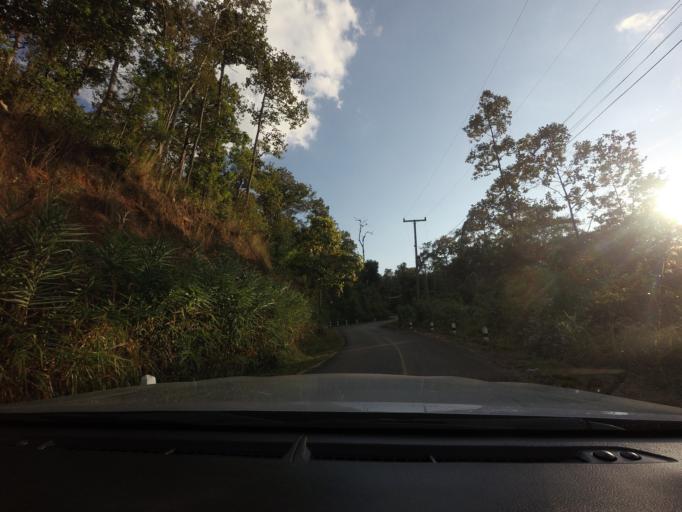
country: TH
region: Chiang Mai
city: Phrao
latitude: 19.4898
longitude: 99.1674
